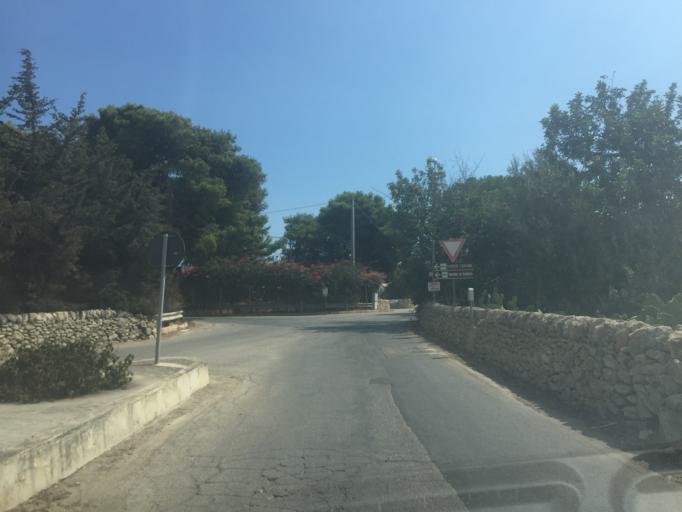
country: IT
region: Sicily
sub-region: Ragusa
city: Santa Croce Camerina
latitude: 36.8072
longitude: 14.5155
